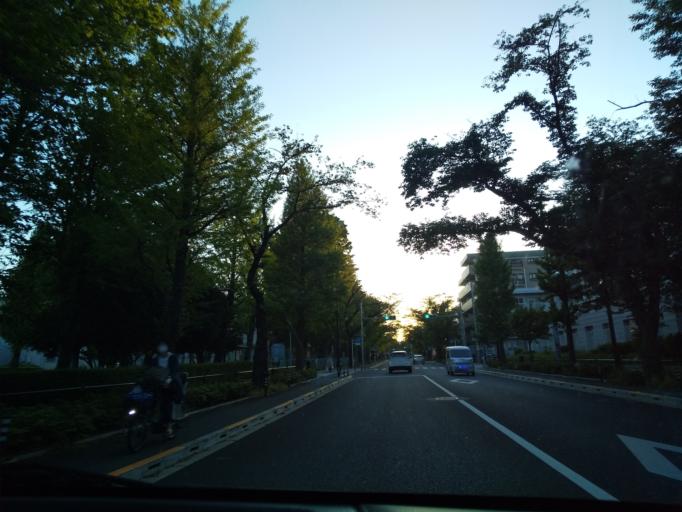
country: JP
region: Tokyo
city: Kokubunji
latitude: 35.6863
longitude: 139.4435
